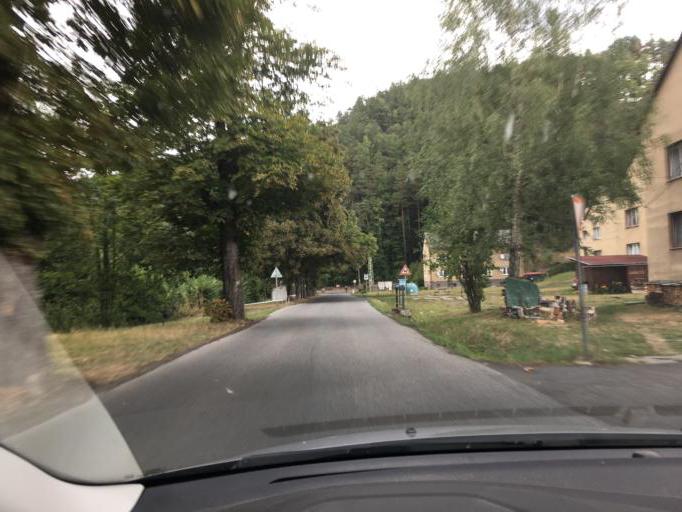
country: CZ
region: Ustecky
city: Ceska Kamenice
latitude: 50.8067
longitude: 14.3599
